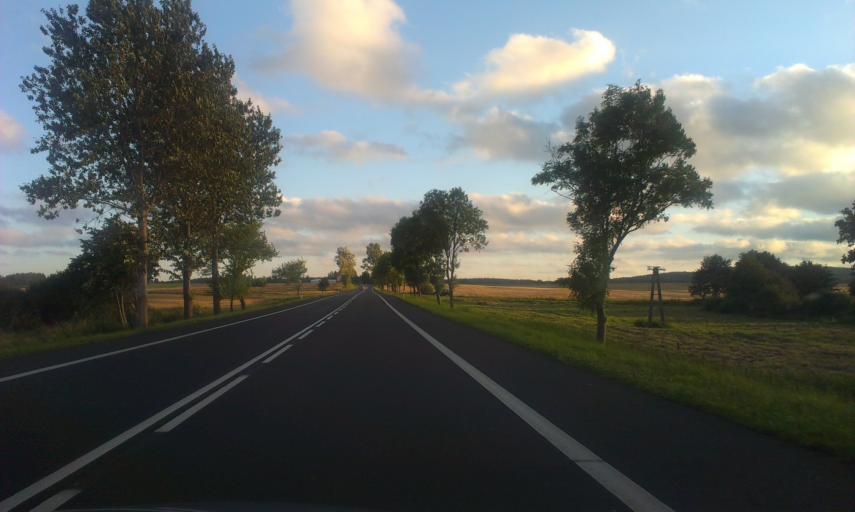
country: PL
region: West Pomeranian Voivodeship
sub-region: Powiat slawienski
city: Darlowo
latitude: 54.2887
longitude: 16.4917
